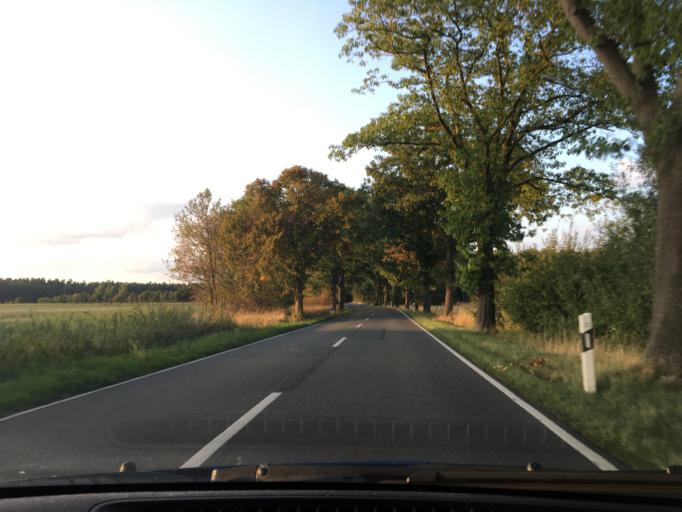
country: DE
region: Lower Saxony
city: Bleckede
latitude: 53.2643
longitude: 10.7436
